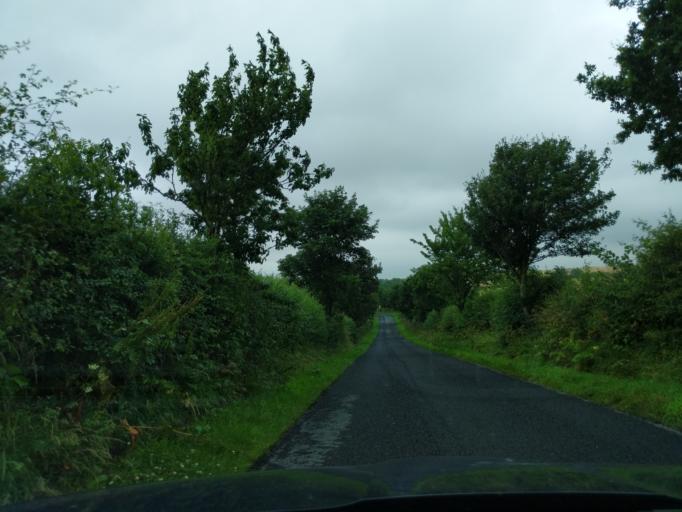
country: GB
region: England
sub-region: Northumberland
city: Ford
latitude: 55.7011
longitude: -2.1440
